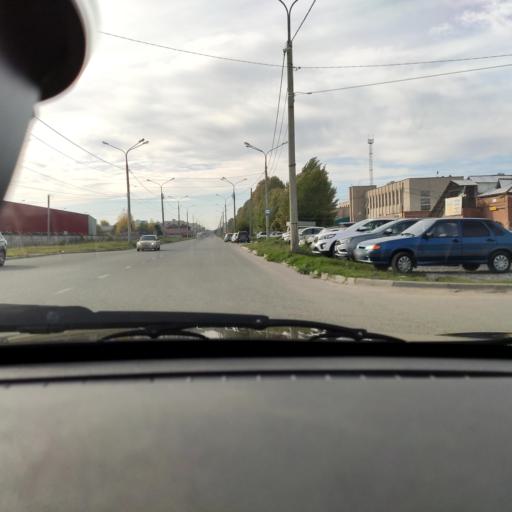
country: RU
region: Samara
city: Tol'yatti
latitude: 53.5417
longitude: 49.4230
